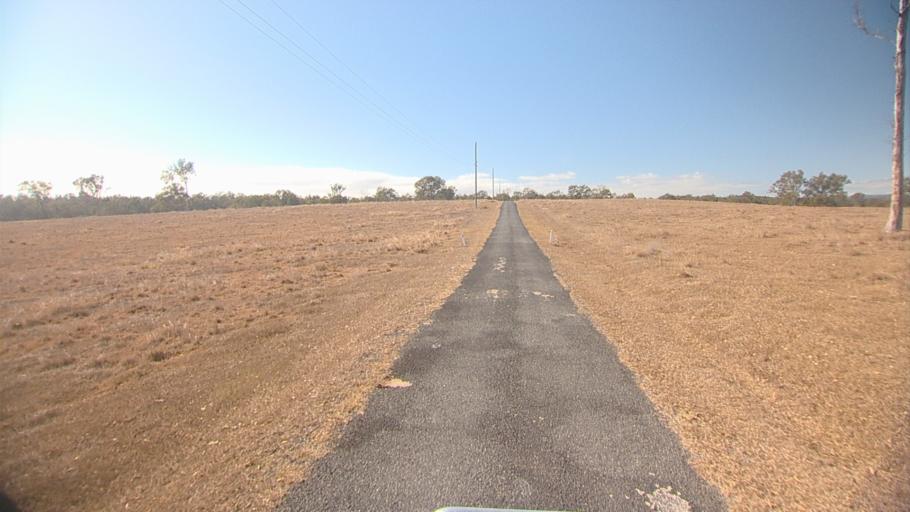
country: AU
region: Queensland
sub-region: Logan
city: North Maclean
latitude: -27.8023
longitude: 153.0186
